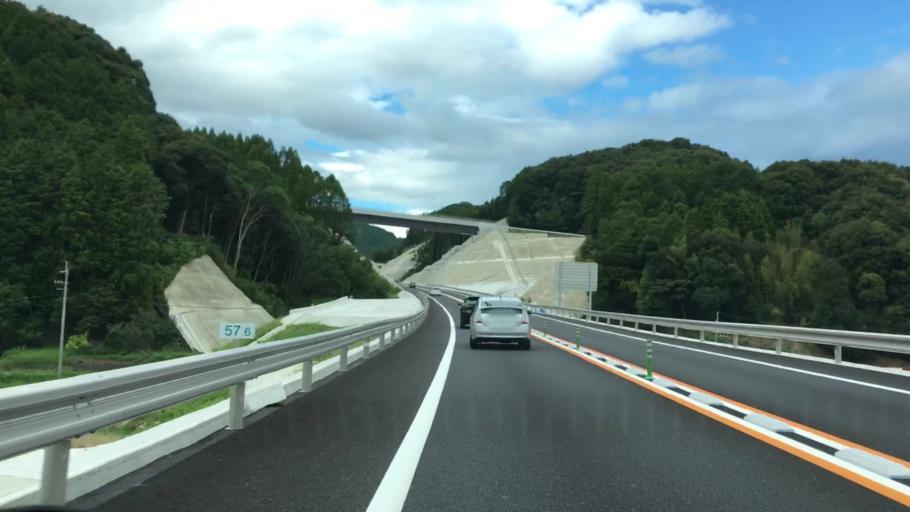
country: JP
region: Saga Prefecture
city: Imaricho-ko
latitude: 33.3017
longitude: 129.9153
